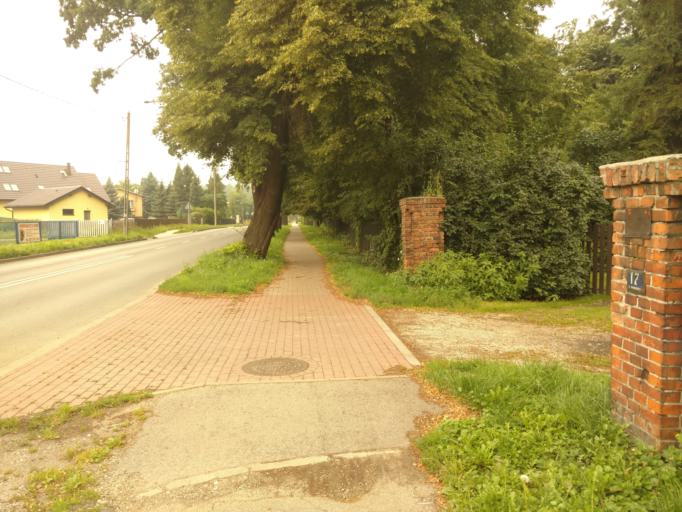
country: PL
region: Silesian Voivodeship
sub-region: Powiat pszczynski
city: Pszczyna
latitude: 49.9884
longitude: 18.9518
